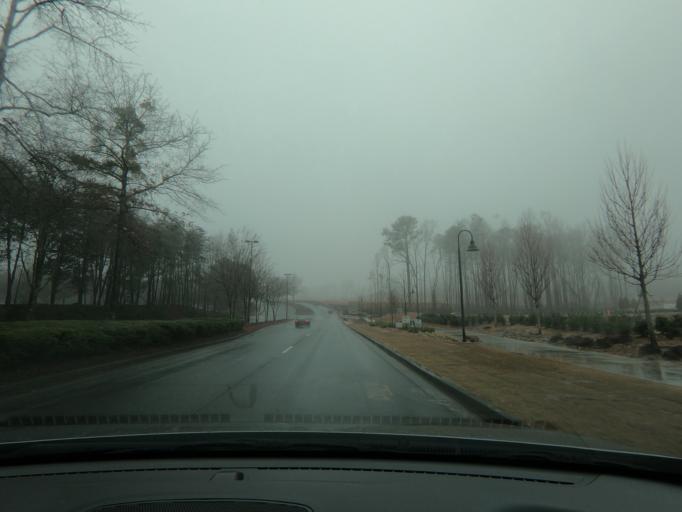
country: US
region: Georgia
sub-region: Fulton County
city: Alpharetta
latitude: 34.0846
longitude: -84.2582
